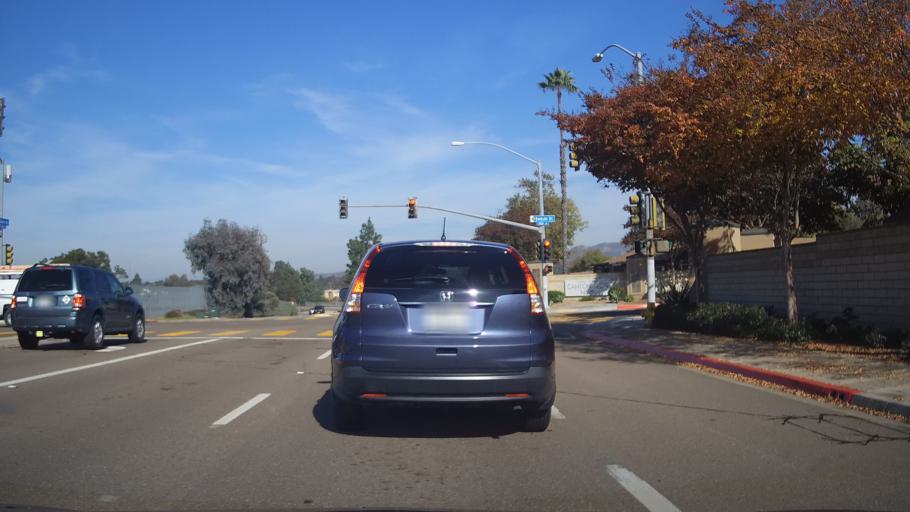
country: US
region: California
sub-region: San Diego County
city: La Mesa
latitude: 32.8160
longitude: -117.1052
